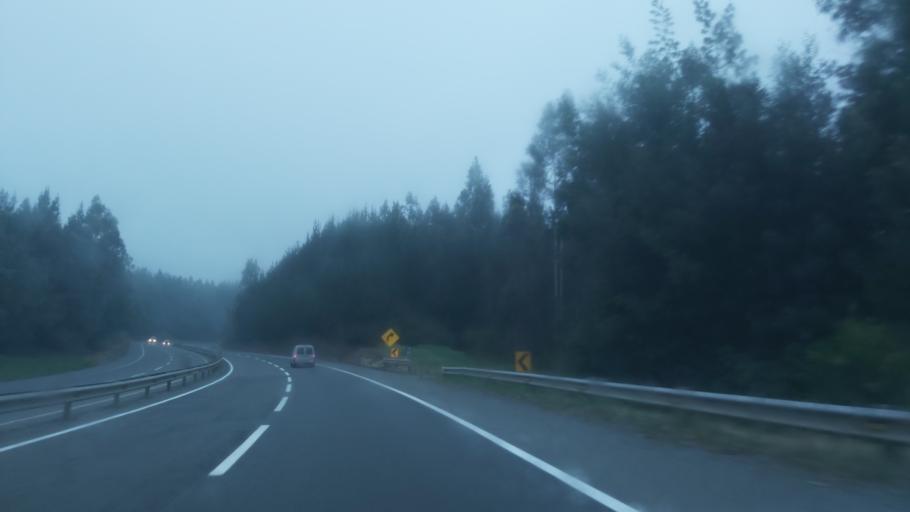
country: CL
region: Biobio
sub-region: Provincia de Concepcion
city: Penco
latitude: -36.7390
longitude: -72.9011
